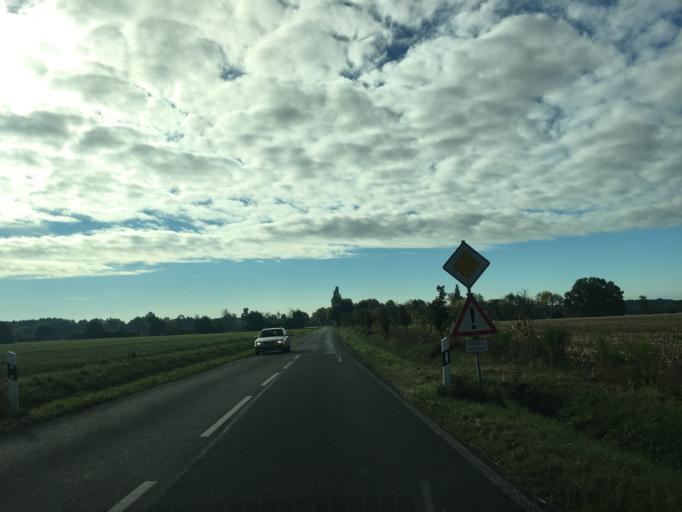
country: DE
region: North Rhine-Westphalia
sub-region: Regierungsbezirk Munster
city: Havixbeck
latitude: 51.9917
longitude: 7.4733
